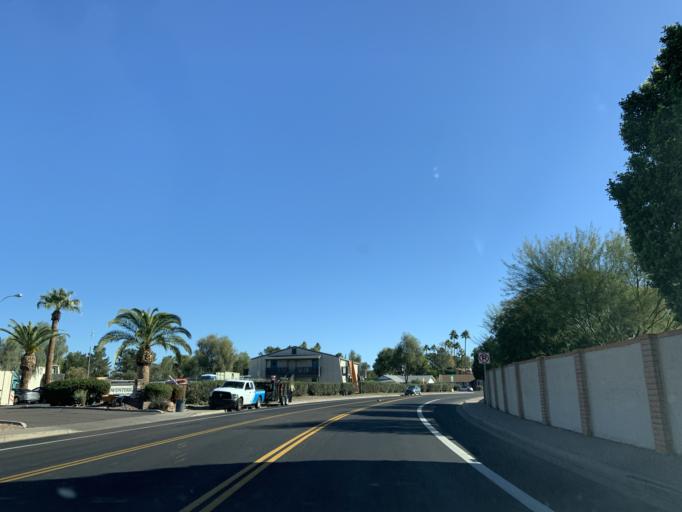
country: US
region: Arizona
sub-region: Maricopa County
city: San Carlos
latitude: 33.3677
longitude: -111.8765
